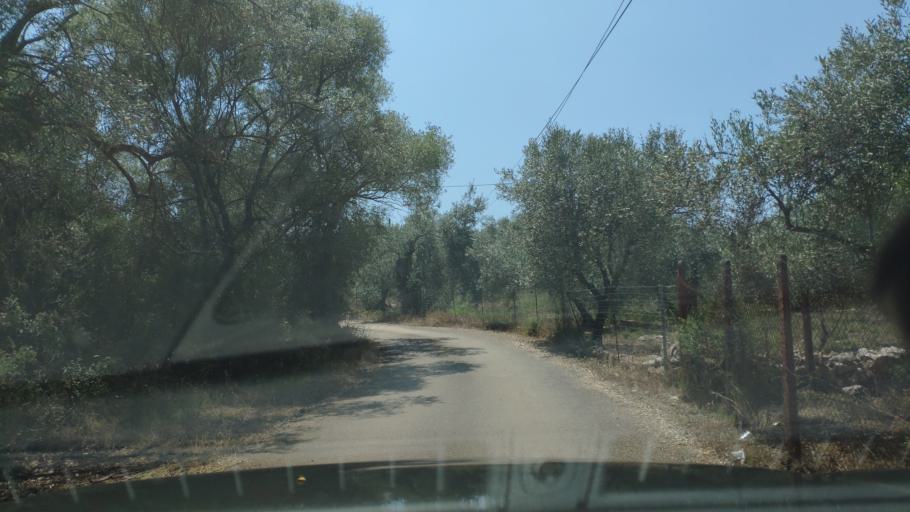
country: GR
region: West Greece
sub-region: Nomos Aitolias kai Akarnanias
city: Amfilochia
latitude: 38.9035
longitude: 21.1191
